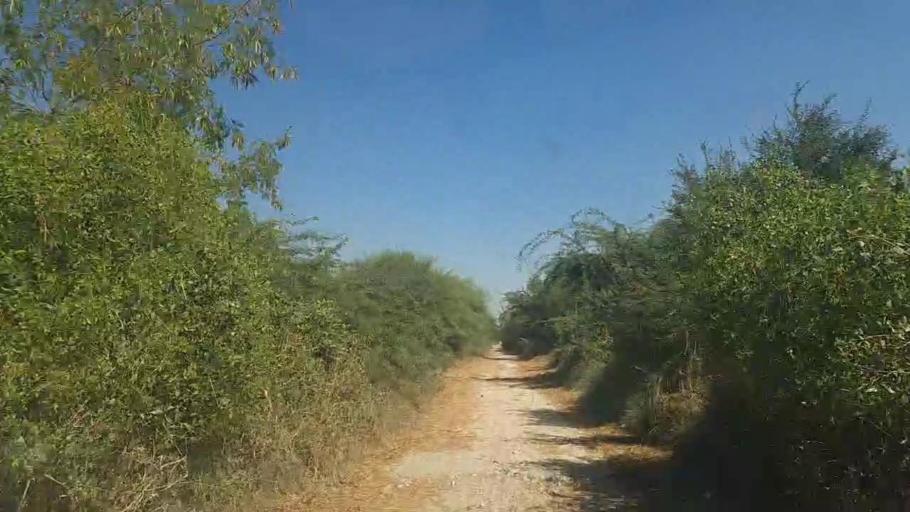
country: PK
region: Sindh
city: Mirpur Batoro
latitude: 24.7021
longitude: 68.2380
